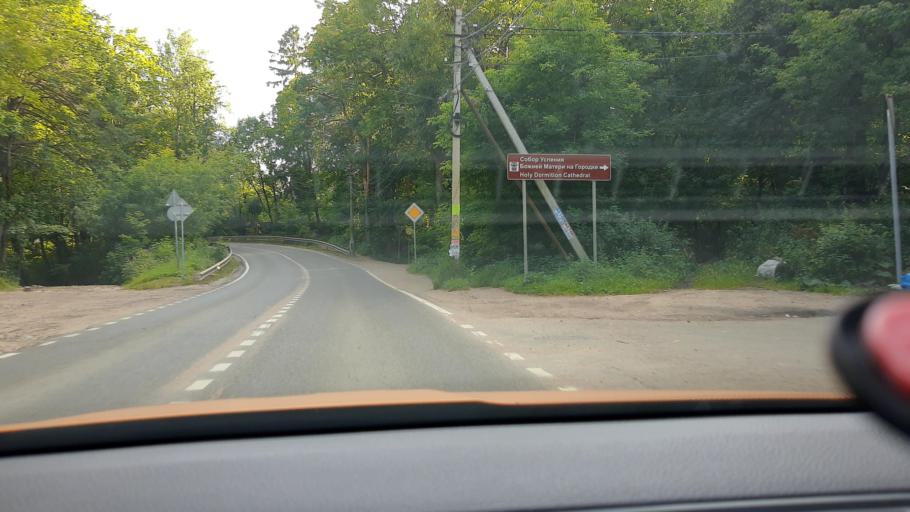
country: RU
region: Moskovskaya
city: Zvenigorod
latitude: 55.7353
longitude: 36.8465
